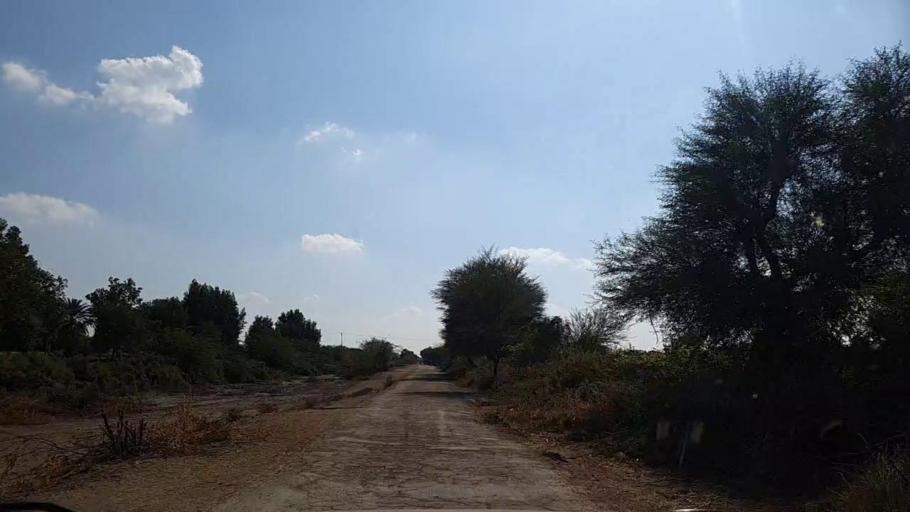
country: PK
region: Sindh
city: Pithoro
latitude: 25.6558
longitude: 69.4487
